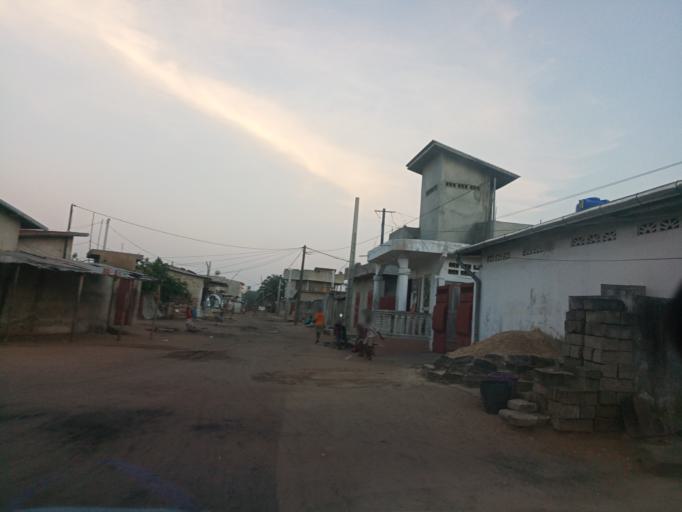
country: BJ
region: Atlantique
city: Hevie
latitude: 6.3934
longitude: 2.2909
